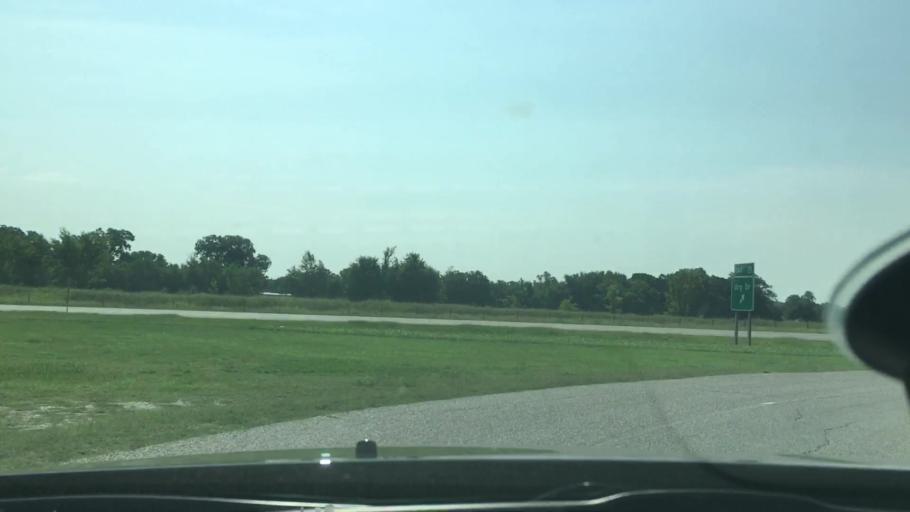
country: US
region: Oklahoma
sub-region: Bryan County
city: Durant
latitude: 34.0556
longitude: -96.3555
